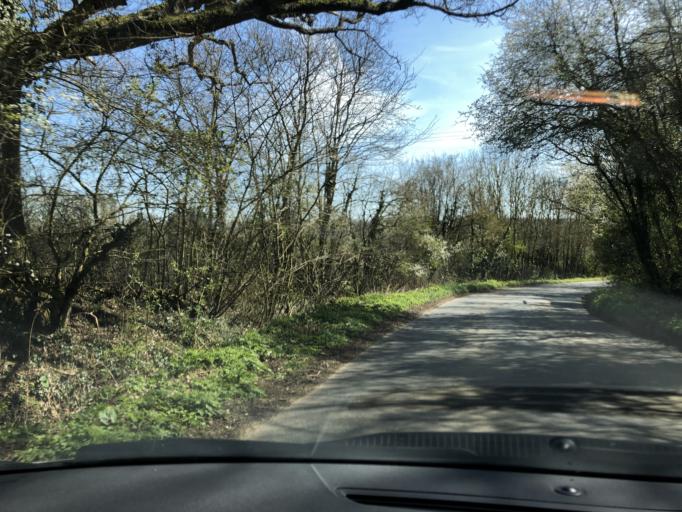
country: GB
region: England
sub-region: Oxfordshire
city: Hook Norton
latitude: 52.0069
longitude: -1.4403
